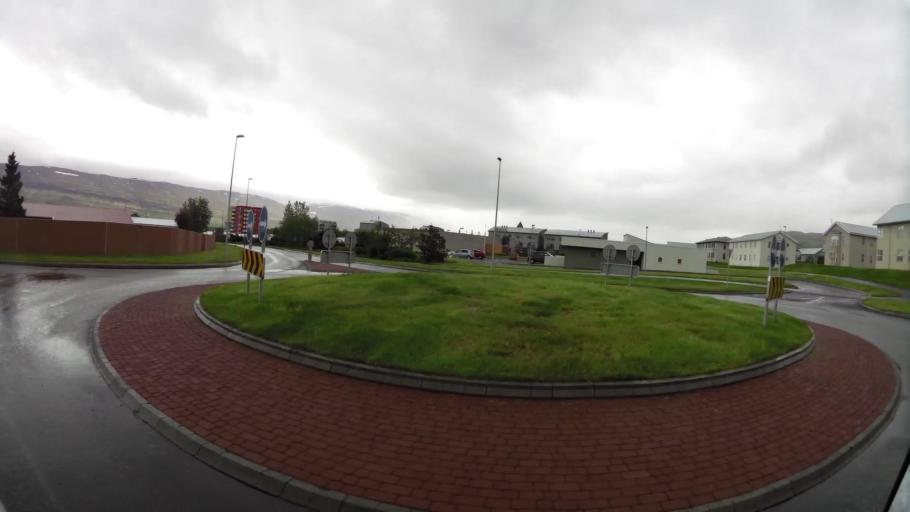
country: IS
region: Northeast
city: Akureyri
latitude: 65.6878
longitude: -18.1371
